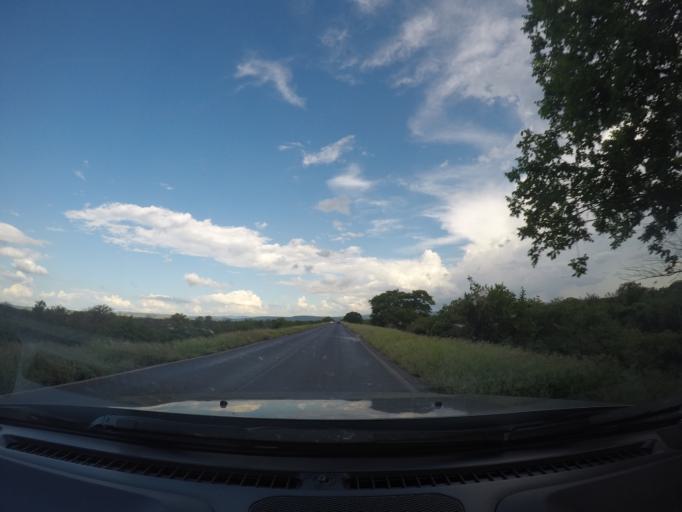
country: BR
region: Bahia
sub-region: Ibotirama
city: Ibotirama
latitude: -12.1646
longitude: -43.2807
